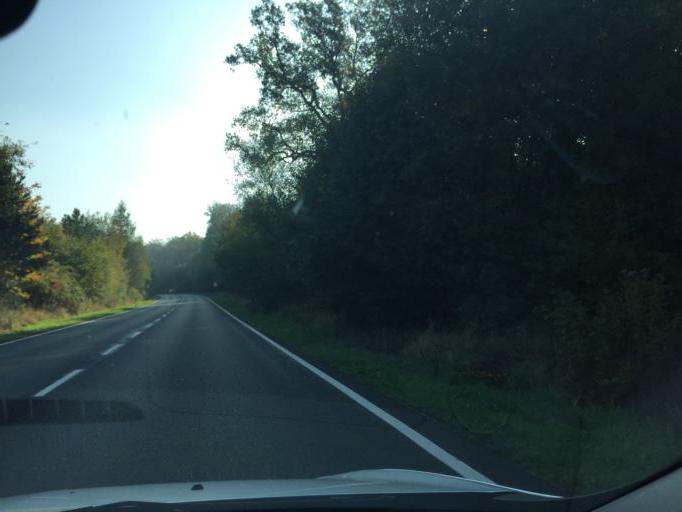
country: LU
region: Luxembourg
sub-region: Canton de Luxembourg
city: Sandweiler
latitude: 49.6100
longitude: 6.2101
